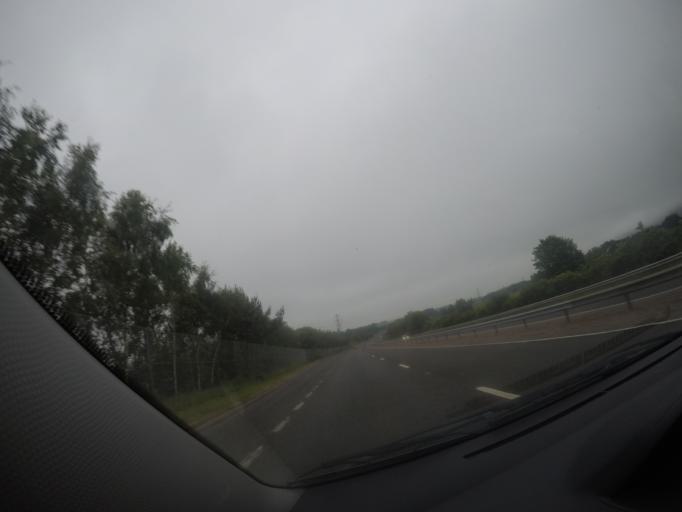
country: GB
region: Scotland
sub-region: Angus
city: Forfar
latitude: 56.5912
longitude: -2.9124
